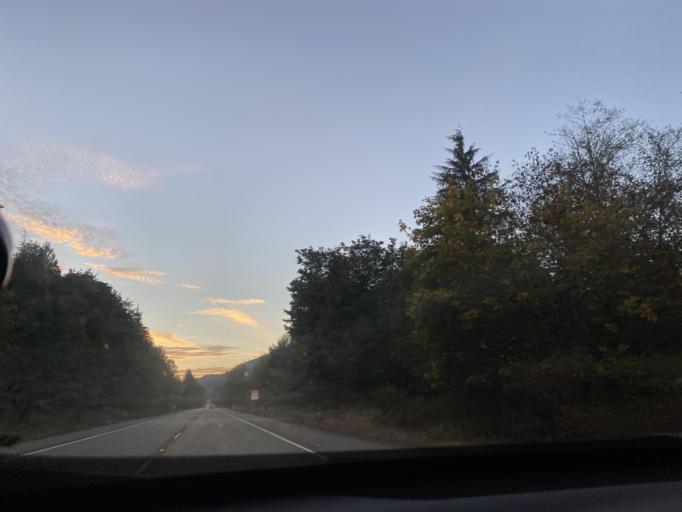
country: US
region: Washington
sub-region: Clallam County
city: Port Angeles
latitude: 48.0652
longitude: -123.6063
